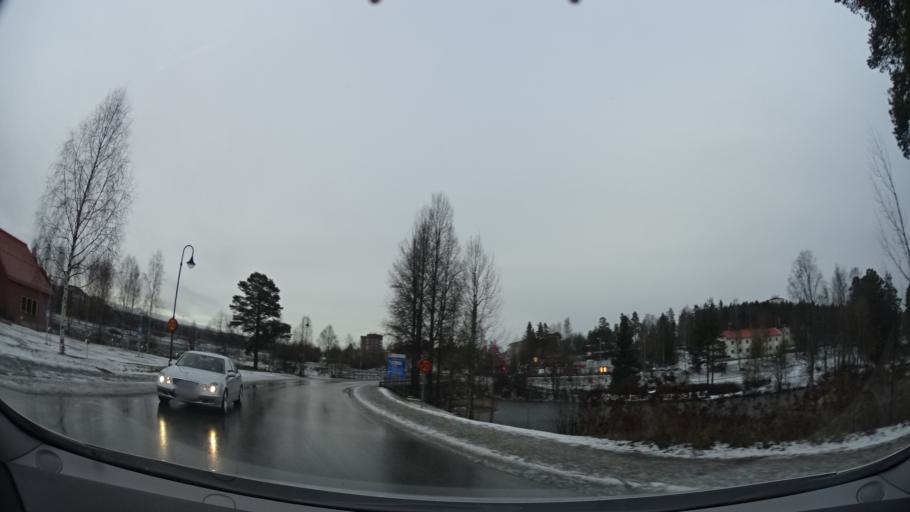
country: SE
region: Vaesterbotten
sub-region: Lycksele Kommun
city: Lycksele
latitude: 64.5934
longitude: 18.6803
